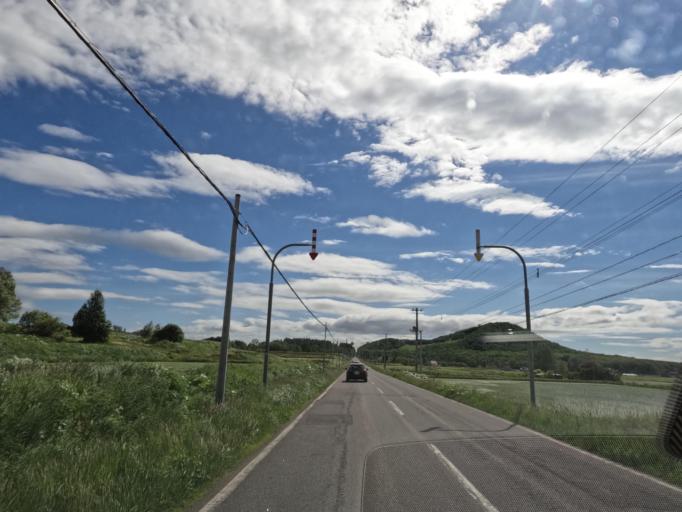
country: JP
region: Hokkaido
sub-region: Asahikawa-shi
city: Asahikawa
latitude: 43.8430
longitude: 142.5494
